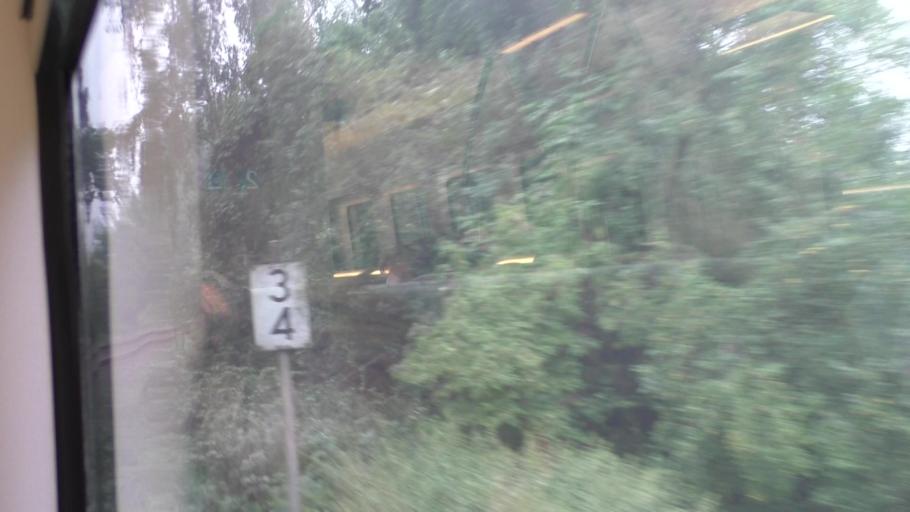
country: DE
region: Saxony
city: Eibau
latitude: 50.9672
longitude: 14.6717
